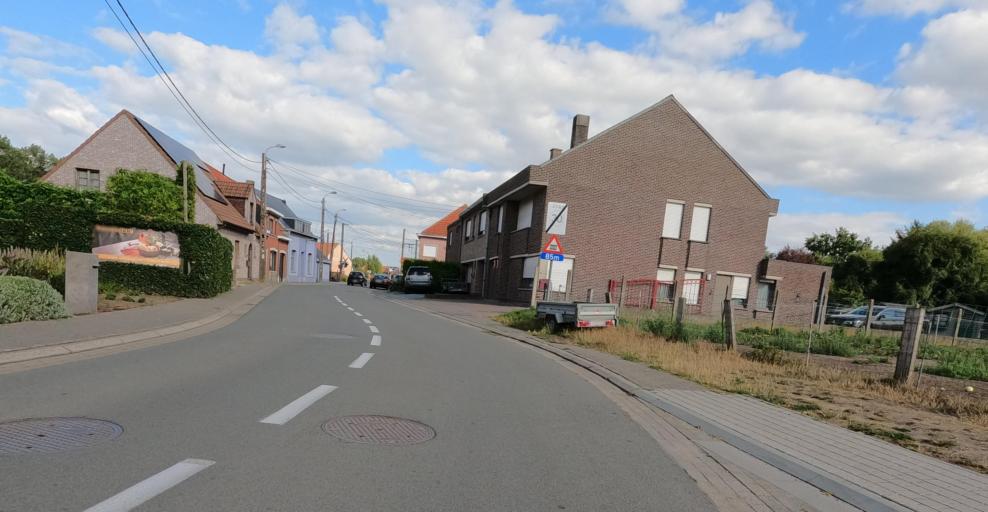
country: BE
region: Flanders
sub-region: Provincie Oost-Vlaanderen
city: Lebbeke
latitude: 51.0020
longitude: 4.1374
